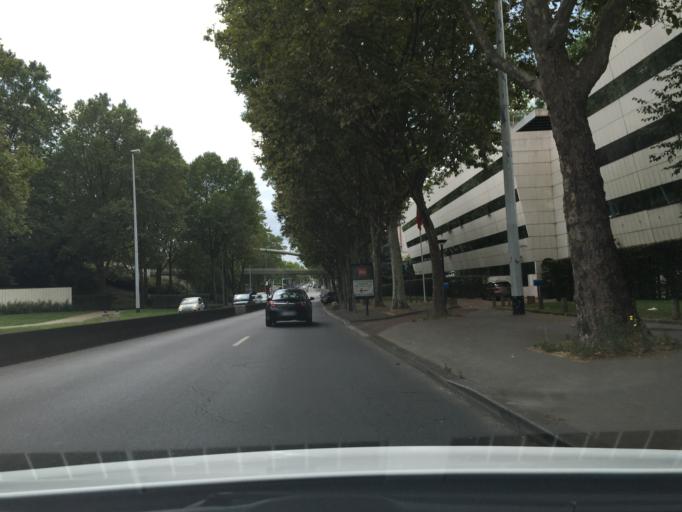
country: FR
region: Ile-de-France
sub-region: Departement des Hauts-de-Seine
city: Nanterre
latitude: 48.8954
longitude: 2.2149
